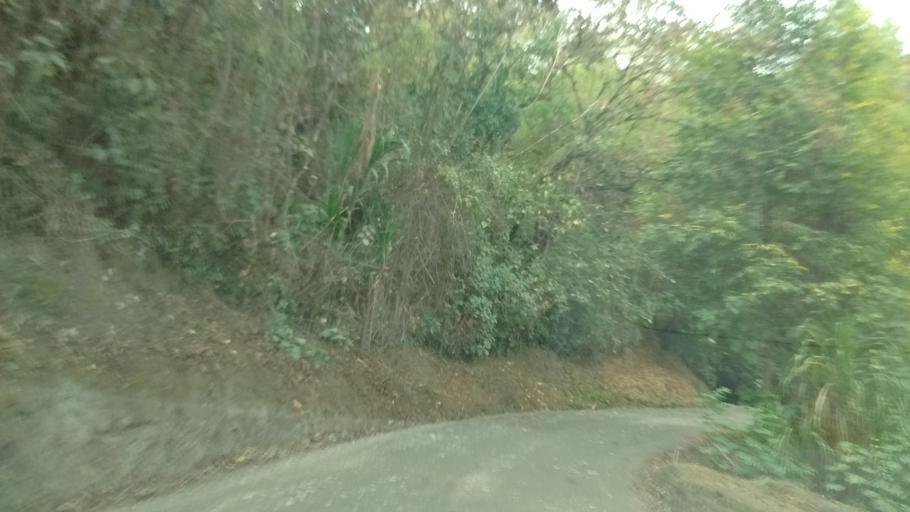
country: CO
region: Cauca
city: Almaguer
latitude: 1.8538
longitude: -76.9295
